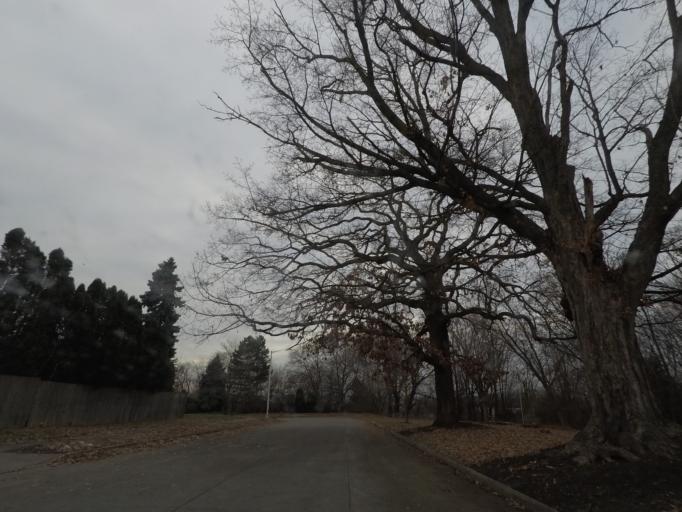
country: US
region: New York
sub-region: Albany County
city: Green Island
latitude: 42.7438
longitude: -73.6670
